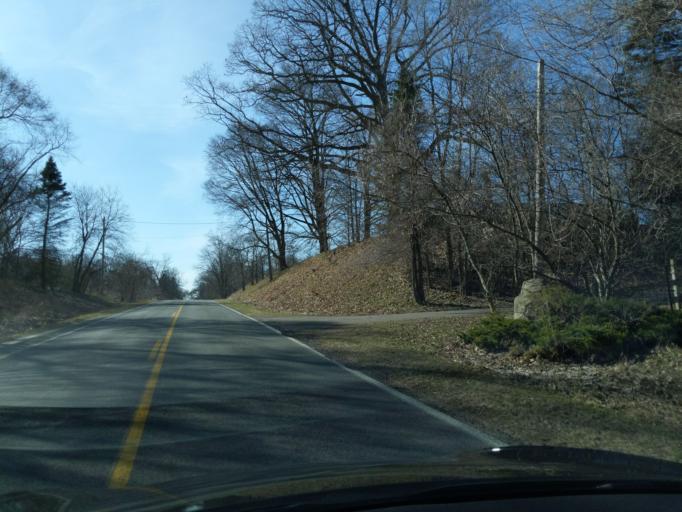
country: US
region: Michigan
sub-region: Ionia County
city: Saranac
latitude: 42.9296
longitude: -85.1856
